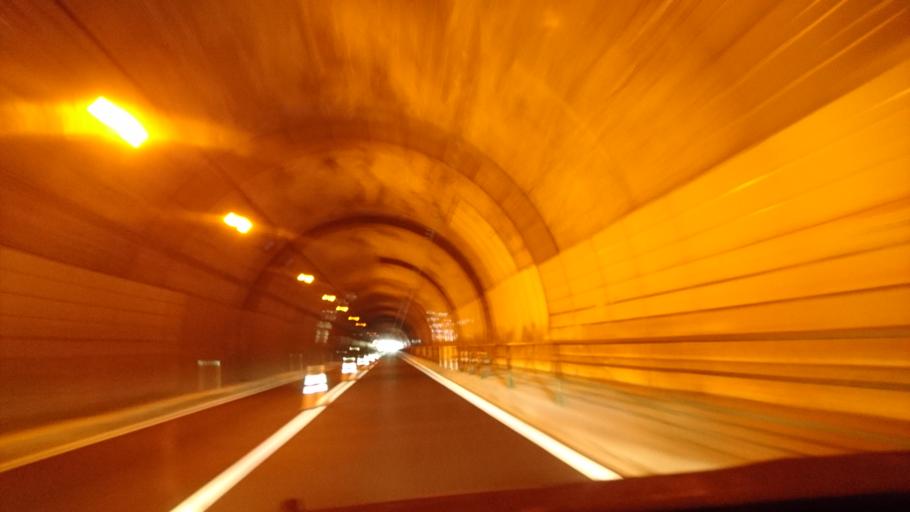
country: JP
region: Akita
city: Yuzawa
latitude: 39.1586
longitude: 140.5417
